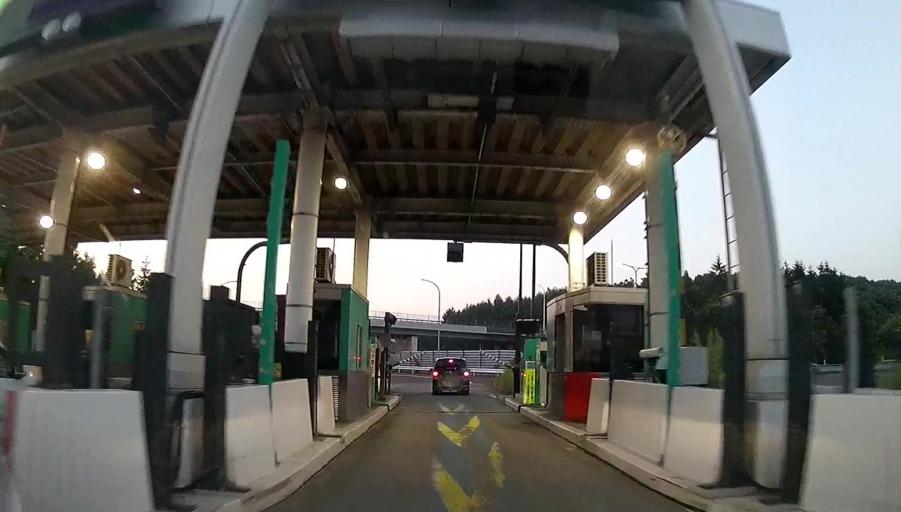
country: JP
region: Hokkaido
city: Kitahiroshima
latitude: 43.0157
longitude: 141.4633
